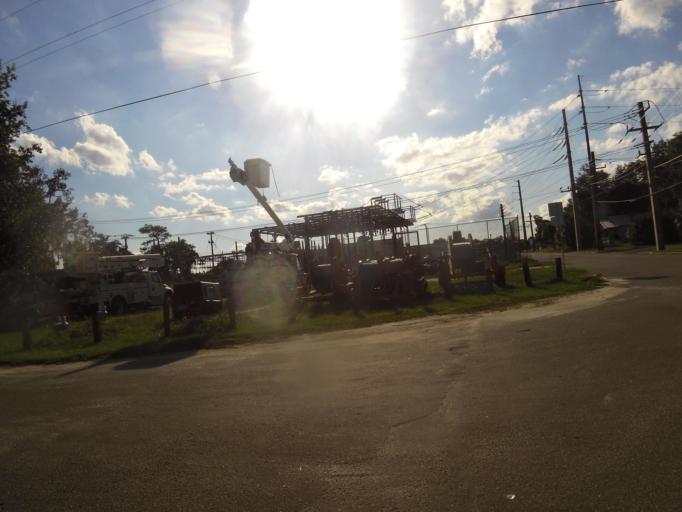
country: US
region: Florida
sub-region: Putnam County
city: Palatka
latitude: 29.6380
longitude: -81.6468
